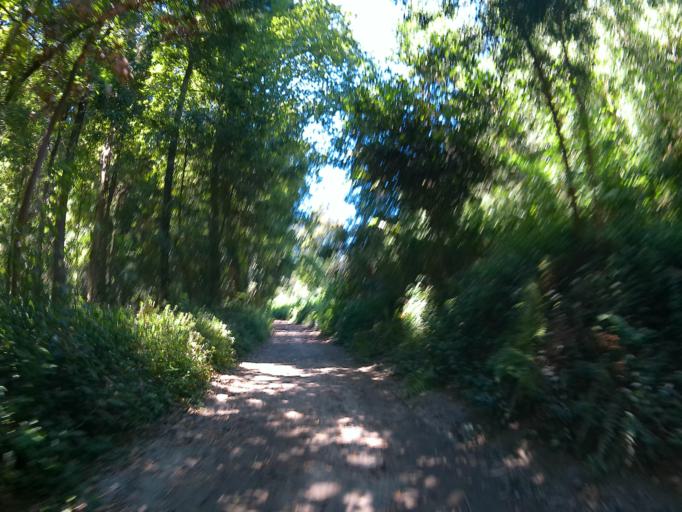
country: PT
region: Viana do Castelo
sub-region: Viana do Castelo
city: Darque
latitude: 41.7073
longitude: -8.7256
